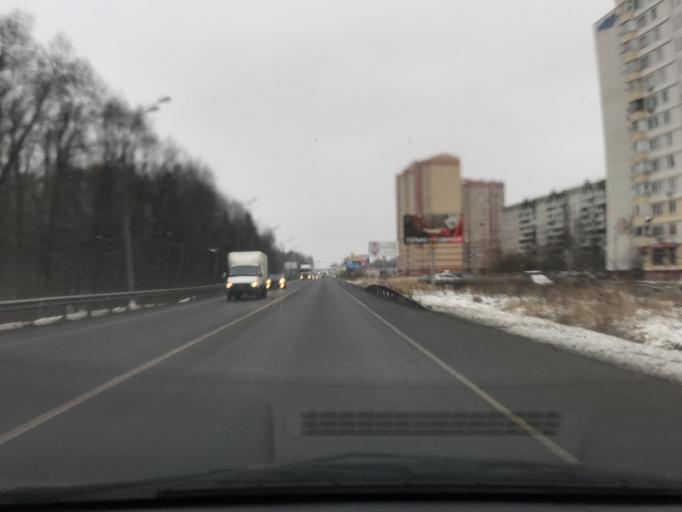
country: RU
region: Moskovskaya
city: Elektrostal'
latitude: 55.8006
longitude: 38.4287
